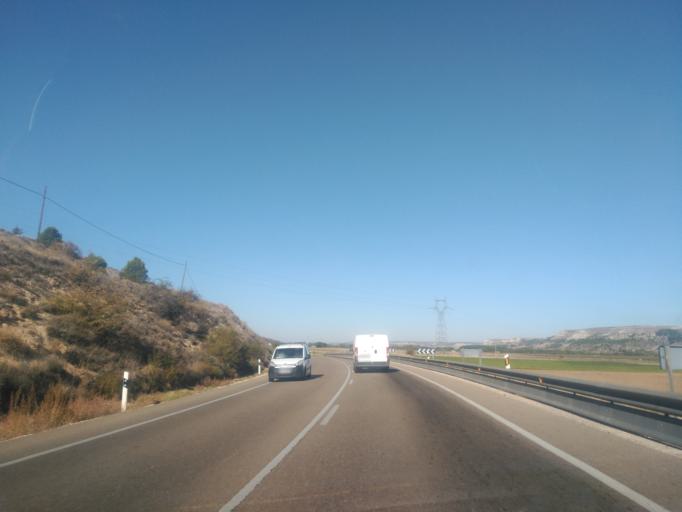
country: ES
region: Castille and Leon
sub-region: Provincia de Valladolid
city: Bocos de Duero
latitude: 41.6082
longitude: -4.0602
